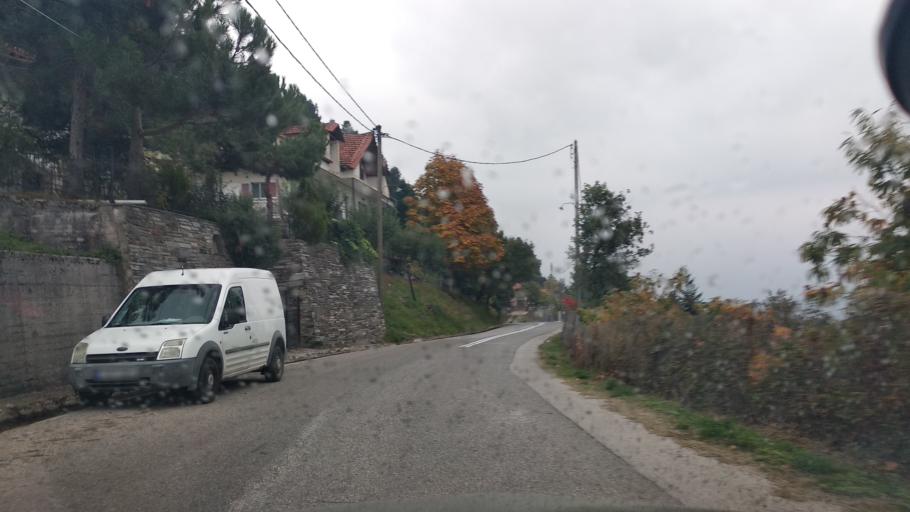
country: GR
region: Thessaly
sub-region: Trikala
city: Pyli
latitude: 39.5071
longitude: 21.5341
